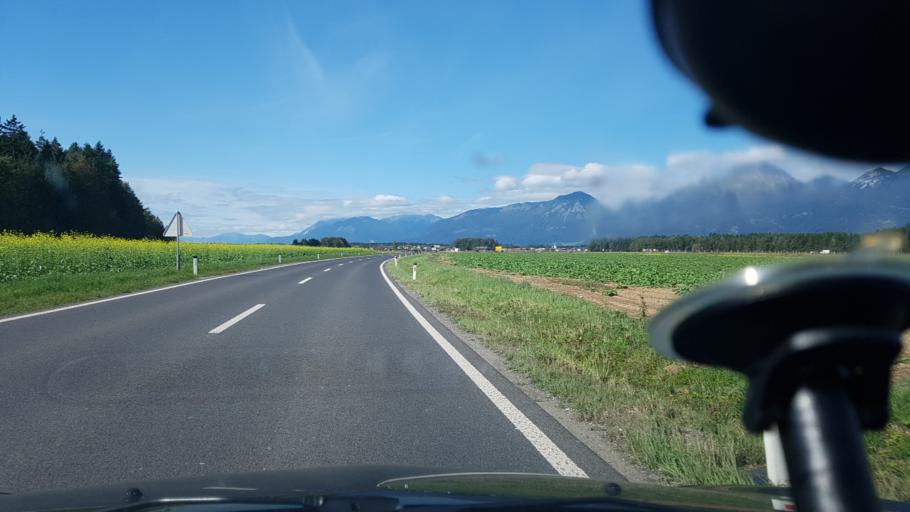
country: SI
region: Sencur
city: Sencur
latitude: 46.2312
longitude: 14.4347
